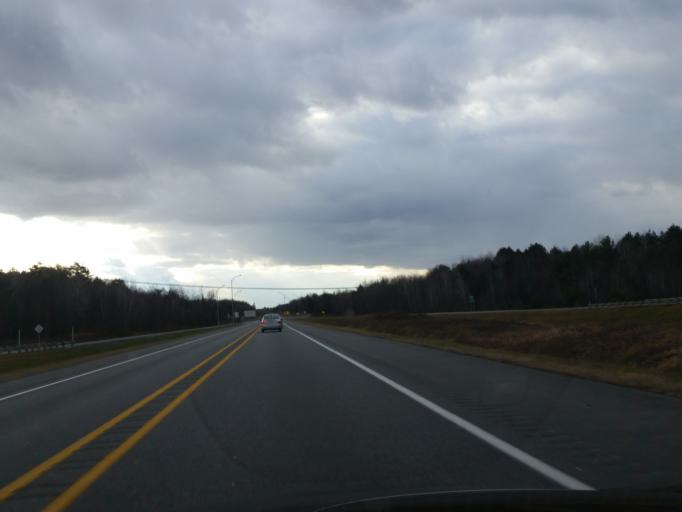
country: CA
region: Quebec
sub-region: Laurentides
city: Saint-Colomban
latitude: 45.6739
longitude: -74.1854
